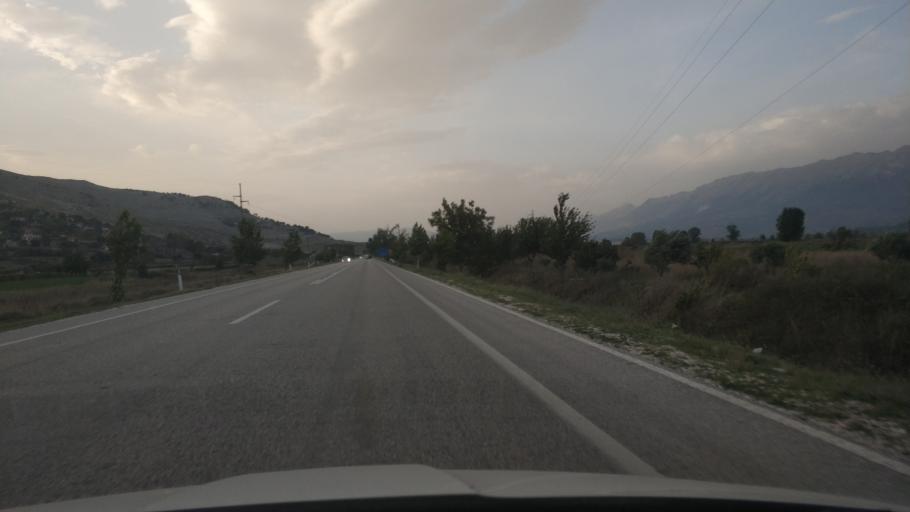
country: AL
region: Gjirokaster
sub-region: Rrethi i Gjirokastres
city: Libohove
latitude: 39.9612
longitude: 20.2449
